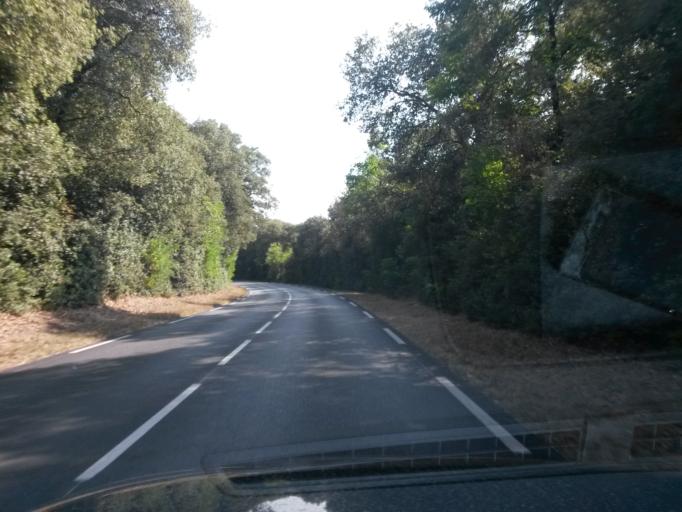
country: FR
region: Pays de la Loire
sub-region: Departement de la Vendee
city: Olonne-sur-Mer
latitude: 46.5736
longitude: -1.8234
